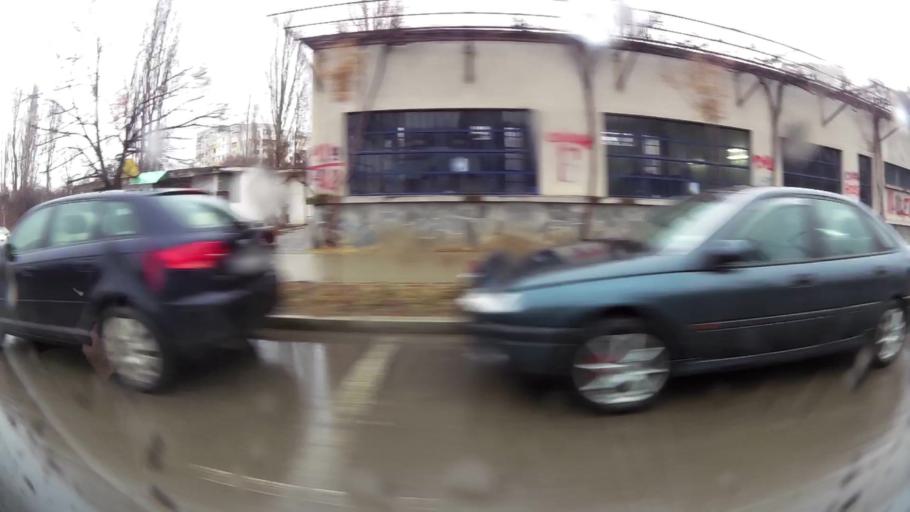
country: BG
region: Sofia-Capital
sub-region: Stolichna Obshtina
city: Sofia
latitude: 42.6494
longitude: 23.3994
